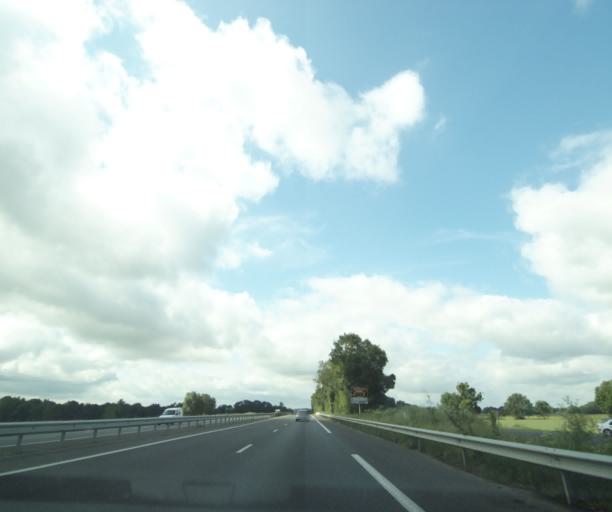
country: FR
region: Pays de la Loire
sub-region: Departement de Maine-et-Loire
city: Vivy
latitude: 47.2982
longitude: -0.0394
